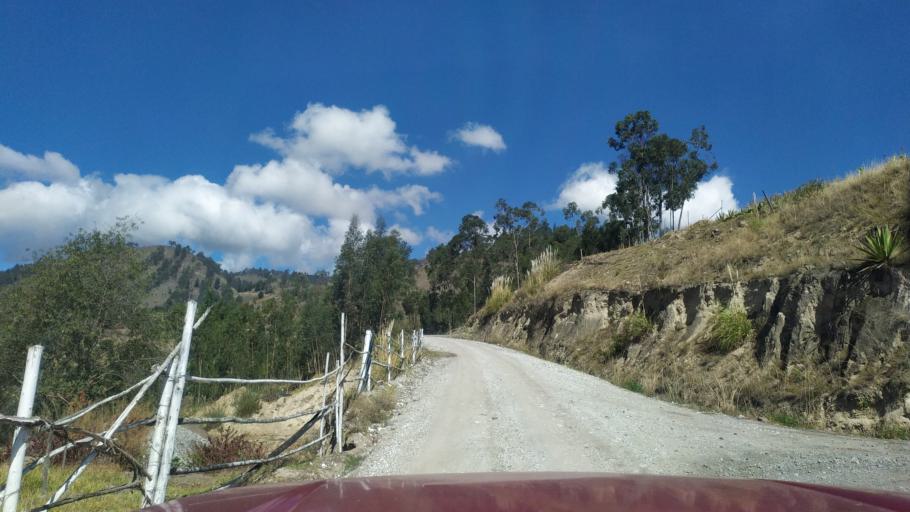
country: EC
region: Chimborazo
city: Riobamba
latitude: -1.6813
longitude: -78.6914
